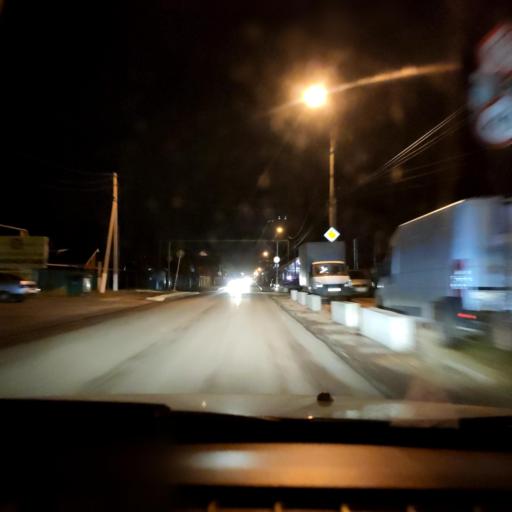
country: RU
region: Samara
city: Podstepki
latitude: 53.5103
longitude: 49.2401
